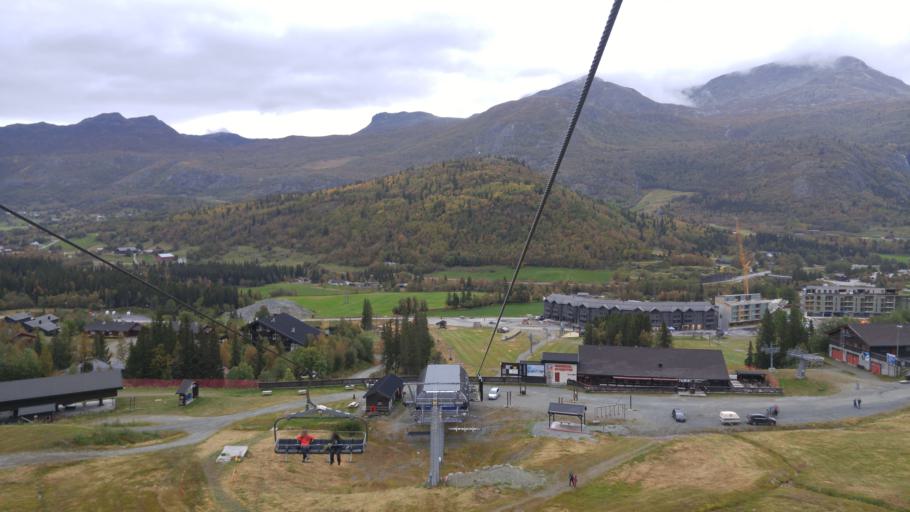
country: NO
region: Buskerud
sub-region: Hemsedal
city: Hemsedal
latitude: 60.8589
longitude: 8.5133
